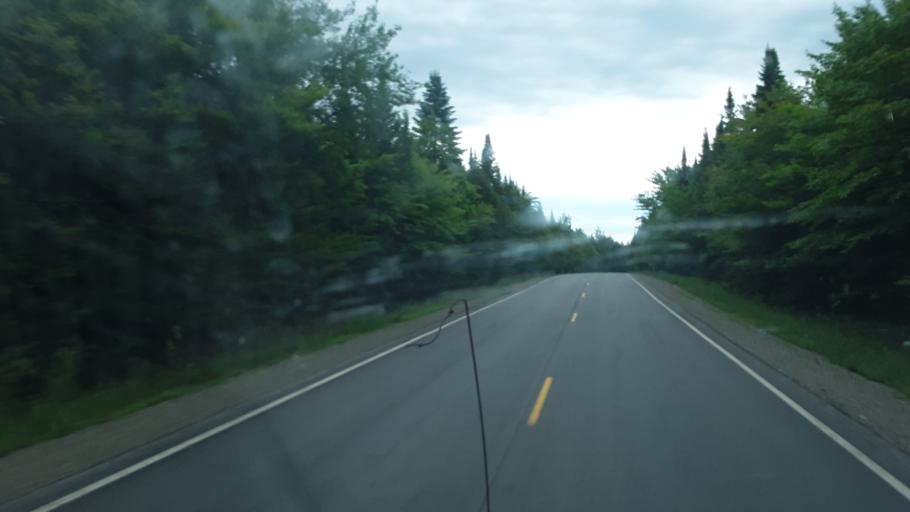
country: US
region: Maine
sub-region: Penobscot County
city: Medway
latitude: 45.7457
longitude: -68.3087
